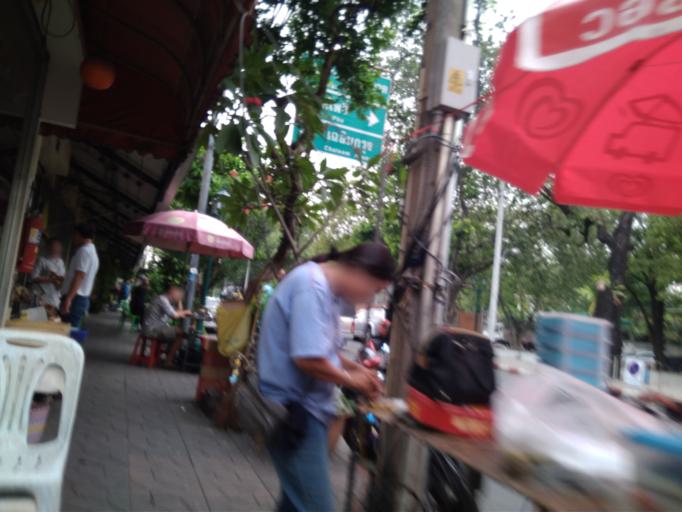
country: TH
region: Bangkok
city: Bangkok
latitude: 13.7482
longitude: 100.4965
